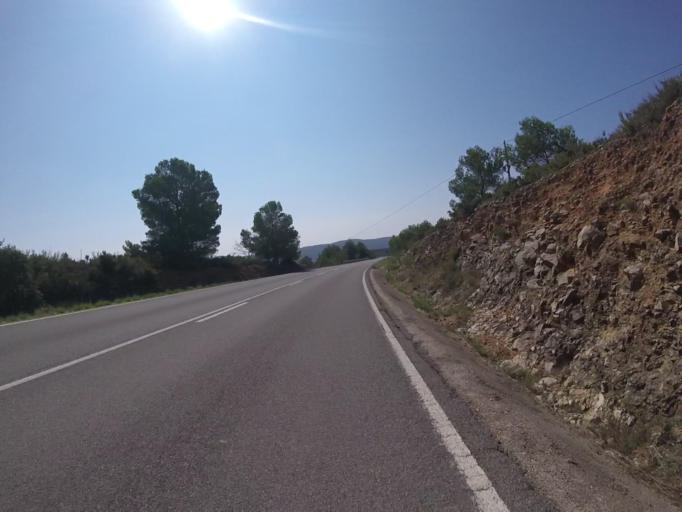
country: ES
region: Valencia
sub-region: Provincia de Castello
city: Adzaneta
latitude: 40.2416
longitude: -0.1893
